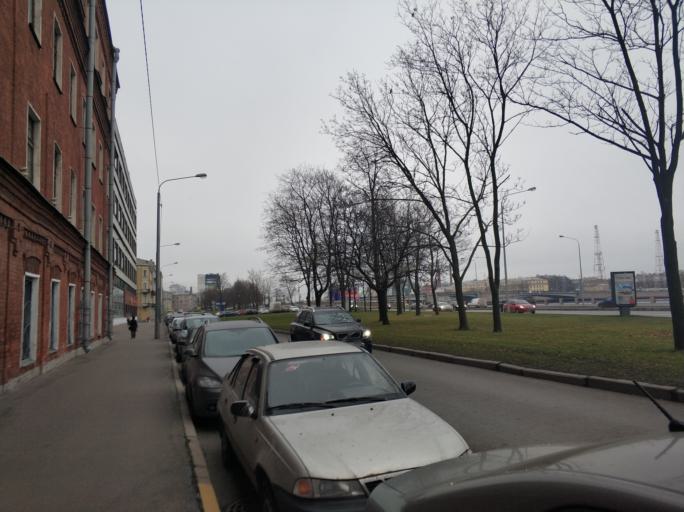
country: RU
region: Leningrad
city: Sampsonievskiy
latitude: 59.9712
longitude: 30.3360
